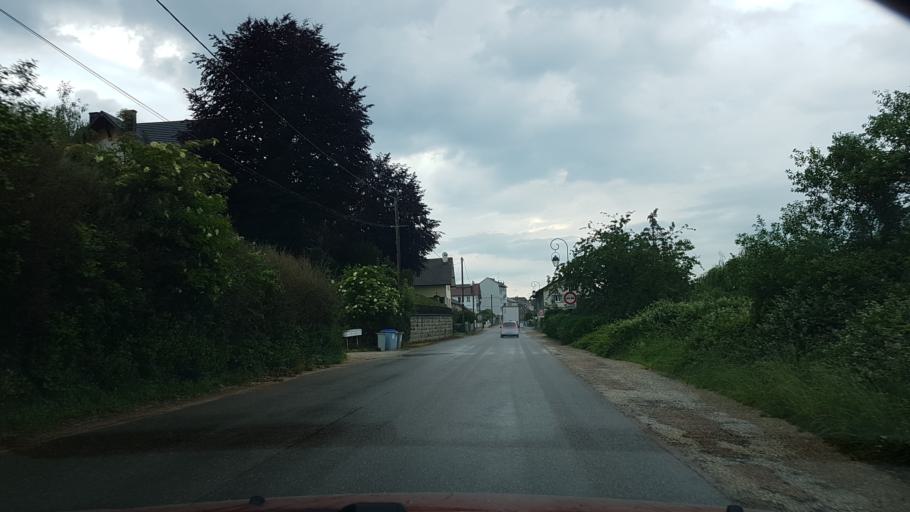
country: FR
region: Franche-Comte
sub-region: Departement du Jura
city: Clairvaux-les-Lacs
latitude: 46.5703
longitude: 5.7454
